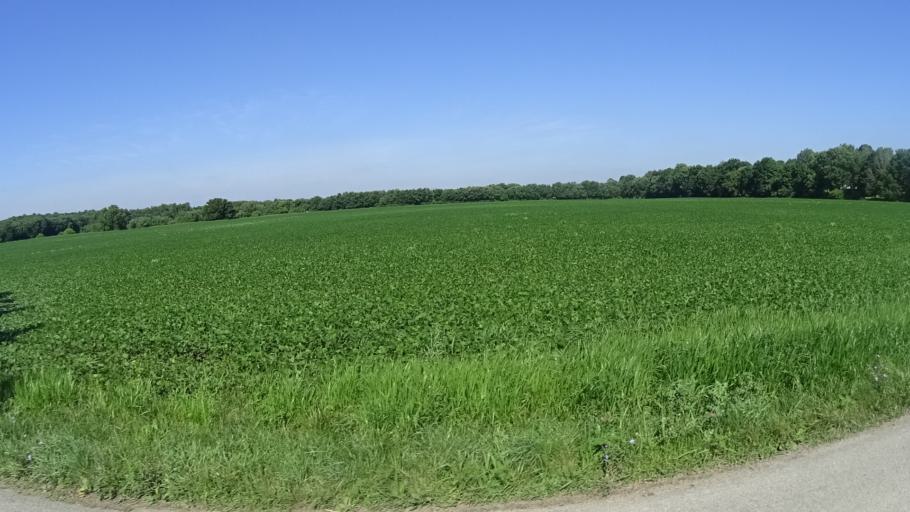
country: US
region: Indiana
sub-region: Madison County
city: Ingalls
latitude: 39.9694
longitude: -85.8151
